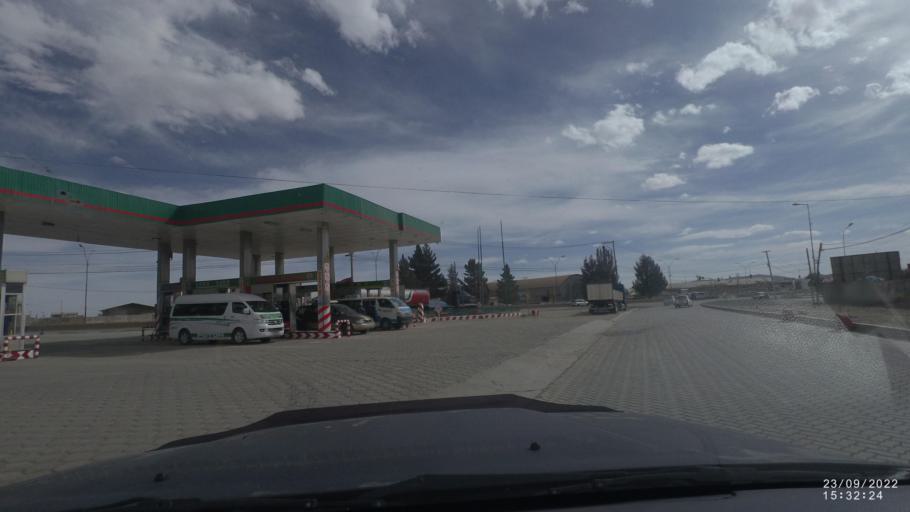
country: BO
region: Oruro
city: Oruro
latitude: -17.9770
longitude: -67.0594
